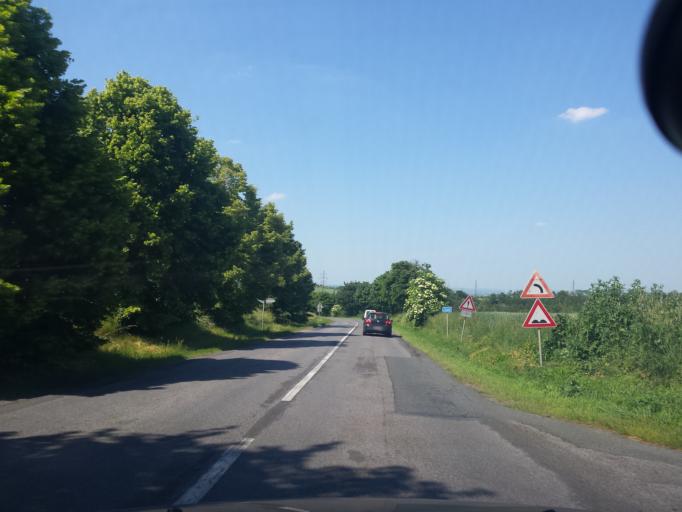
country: CZ
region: Central Bohemia
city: Kralupy nad Vltavou
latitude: 50.2151
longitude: 14.3169
